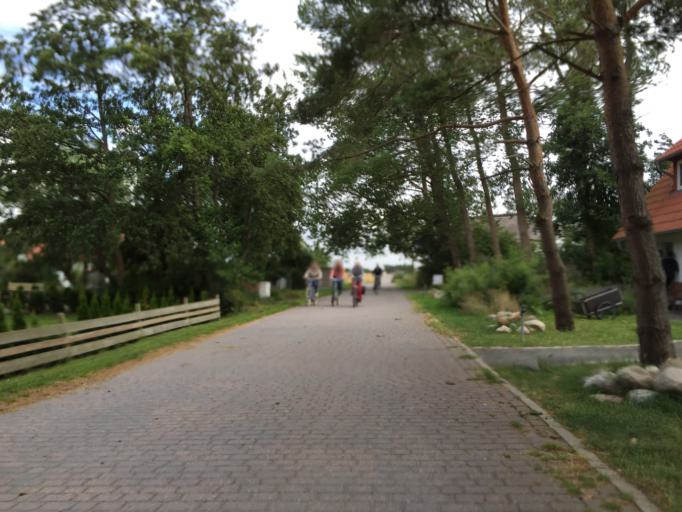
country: DE
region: Mecklenburg-Vorpommern
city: Hiddensee
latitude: 54.5616
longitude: 13.1033
